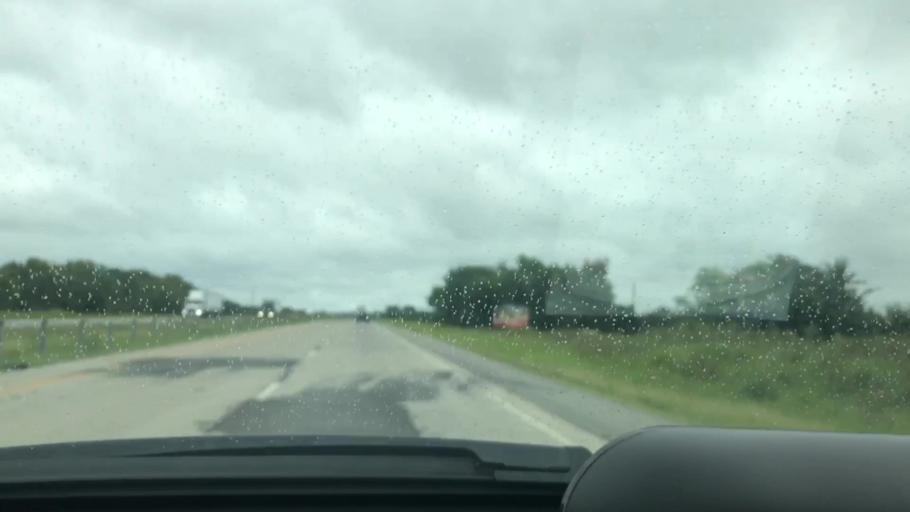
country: US
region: Oklahoma
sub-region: Pittsburg County
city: McAlester
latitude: 34.8078
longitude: -95.8620
